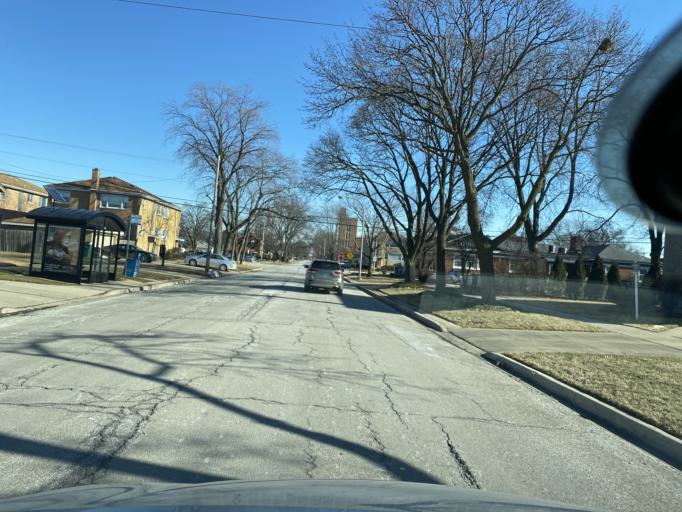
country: US
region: Illinois
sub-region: Cook County
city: Westchester
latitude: 41.8561
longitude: -87.8783
